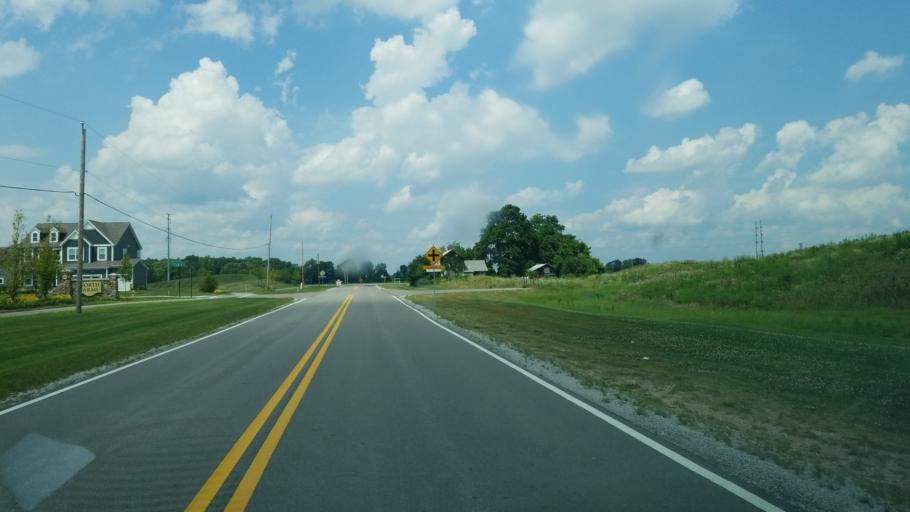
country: US
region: Ohio
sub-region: Delaware County
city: Lewis Center
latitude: 40.2105
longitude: -83.0134
